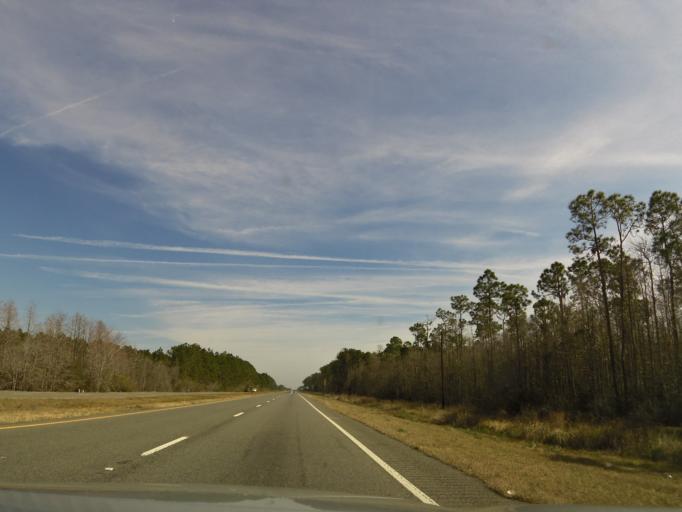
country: US
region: Georgia
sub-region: Pierce County
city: Blackshear
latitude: 31.1702
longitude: -82.2116
